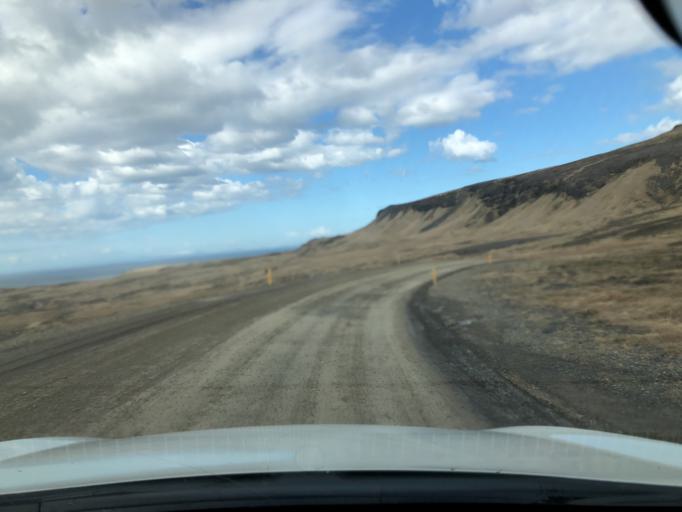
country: IS
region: West
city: Olafsvik
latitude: 64.8825
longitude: -23.5869
